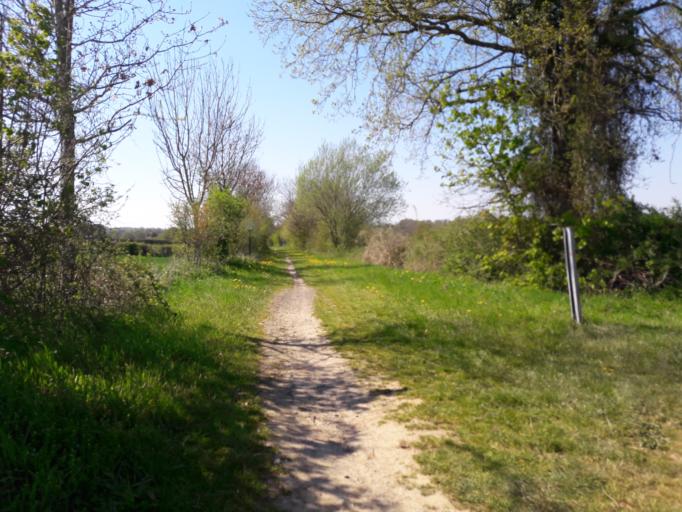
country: FR
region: Nord-Pas-de-Calais
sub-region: Departement du Nord
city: Sains-du-Nord
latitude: 50.1783
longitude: 4.0746
